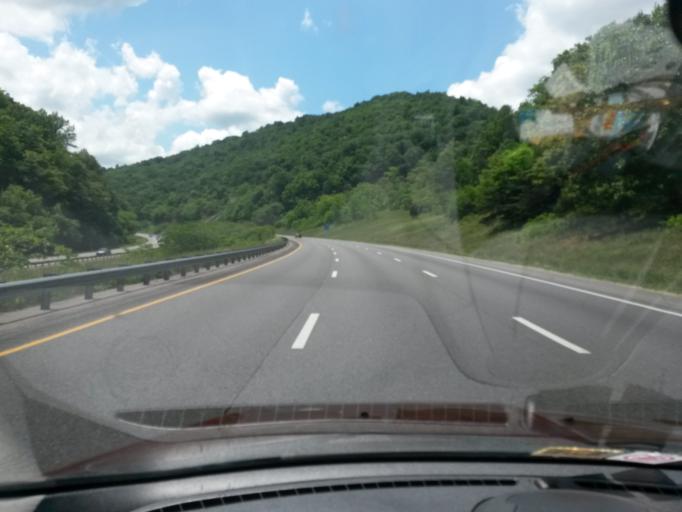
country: US
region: Virginia
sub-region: Montgomery County
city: Shawsville
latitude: 37.2268
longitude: -80.2508
